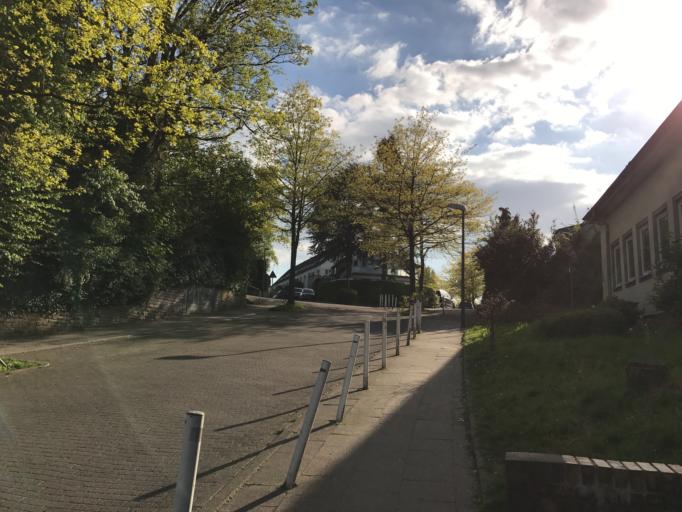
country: DE
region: North Rhine-Westphalia
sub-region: Regierungsbezirk Dusseldorf
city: Essen
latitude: 51.4227
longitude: 7.0308
